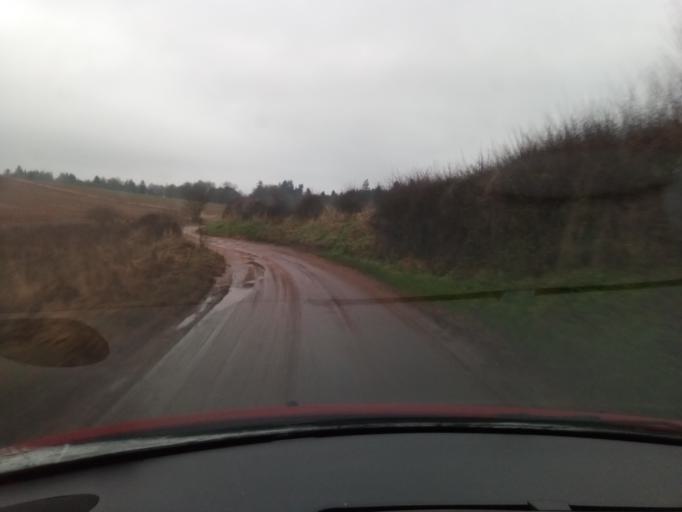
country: GB
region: Scotland
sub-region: The Scottish Borders
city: Kelso
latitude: 55.5474
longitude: -2.4341
